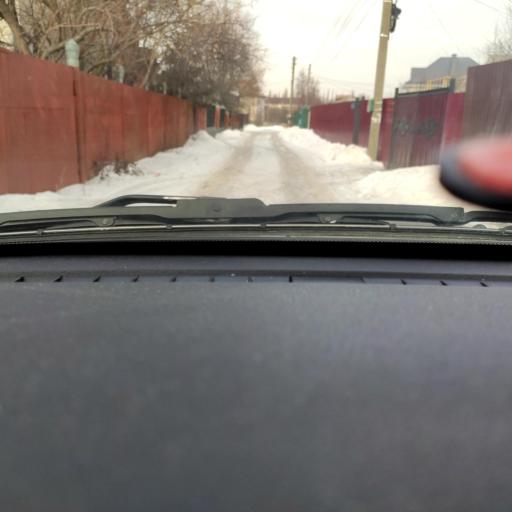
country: RU
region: Voronezj
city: Novaya Usman'
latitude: 51.6214
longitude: 39.3638
